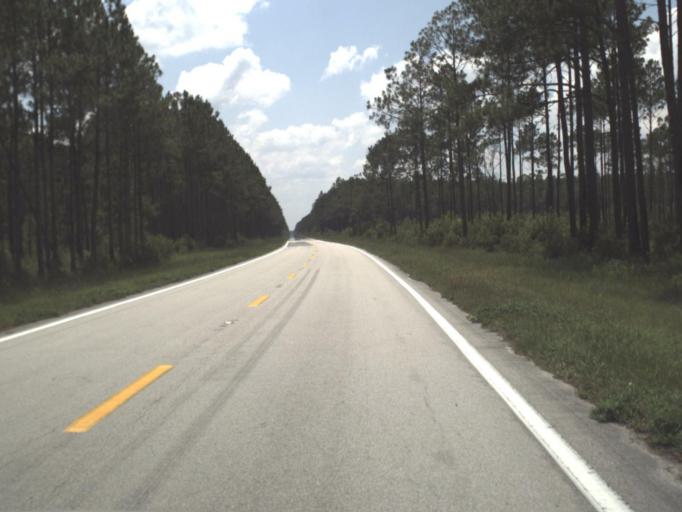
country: US
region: Florida
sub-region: Baker County
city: Macclenny
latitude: 30.5660
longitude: -82.3995
